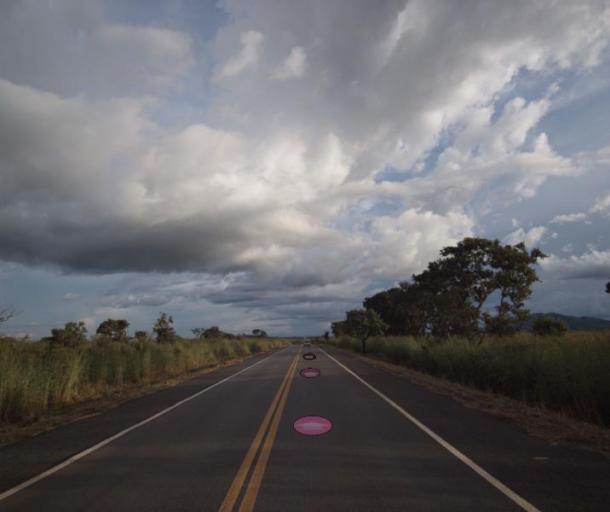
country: BR
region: Goias
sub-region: Barro Alto
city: Barro Alto
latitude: -14.8398
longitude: -48.6383
